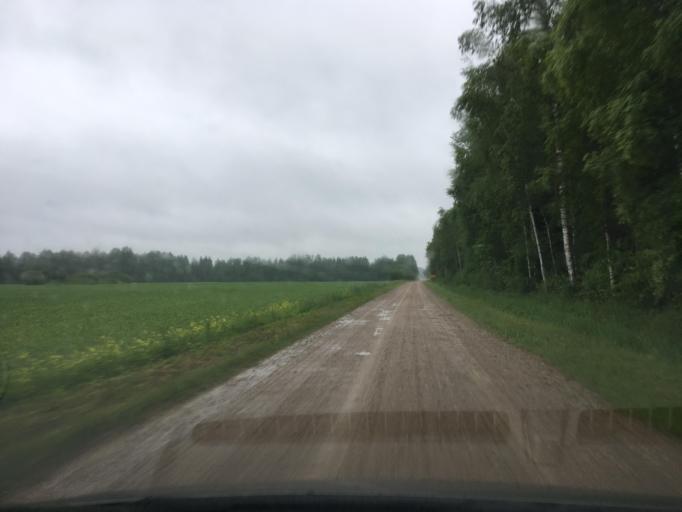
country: EE
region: Laeaene
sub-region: Lihula vald
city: Lihula
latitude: 58.6246
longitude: 23.8190
